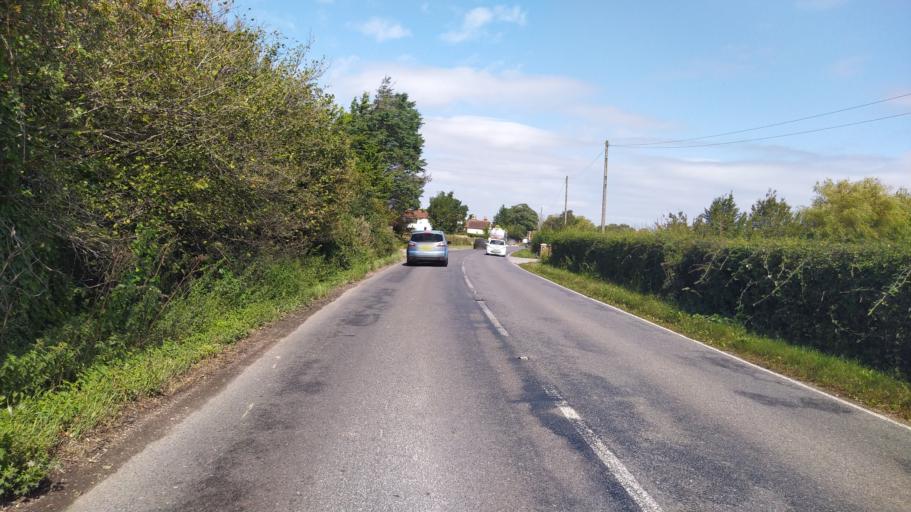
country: GB
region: England
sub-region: West Sussex
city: Chichester
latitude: 50.8174
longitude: -0.7683
